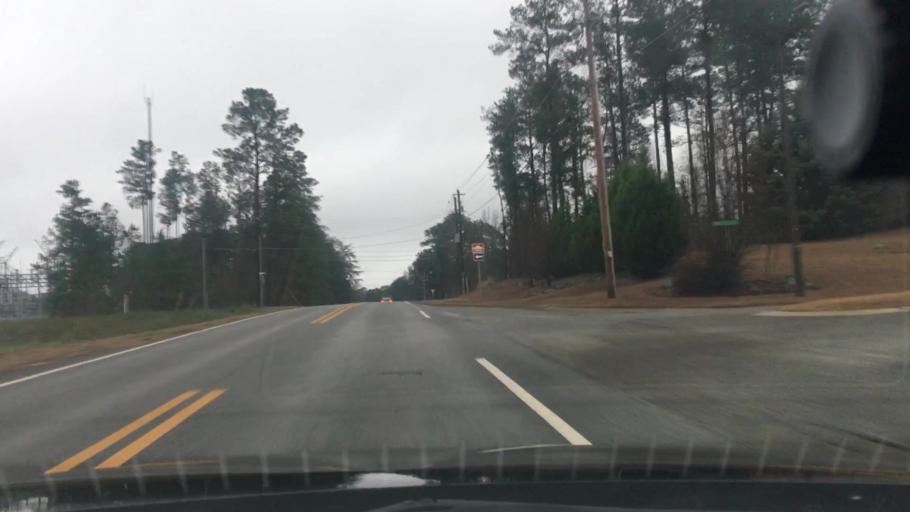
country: US
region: Georgia
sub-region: Bibb County
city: Macon
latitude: 32.9228
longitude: -83.7278
